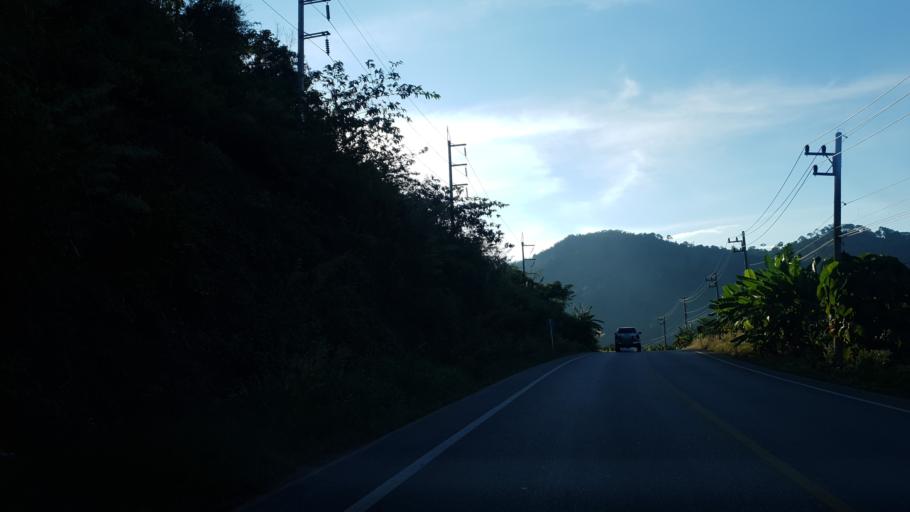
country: TH
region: Loei
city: Dan Sai
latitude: 17.2275
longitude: 101.0400
